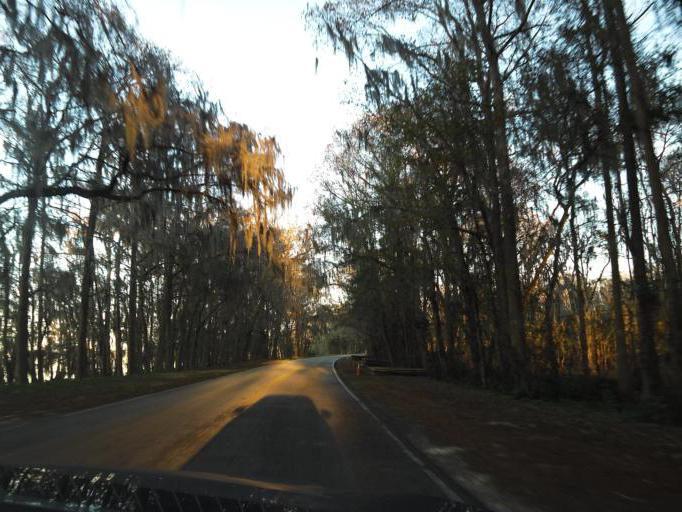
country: US
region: Florida
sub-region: Clay County
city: Green Cove Springs
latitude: 29.9249
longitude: -81.5895
